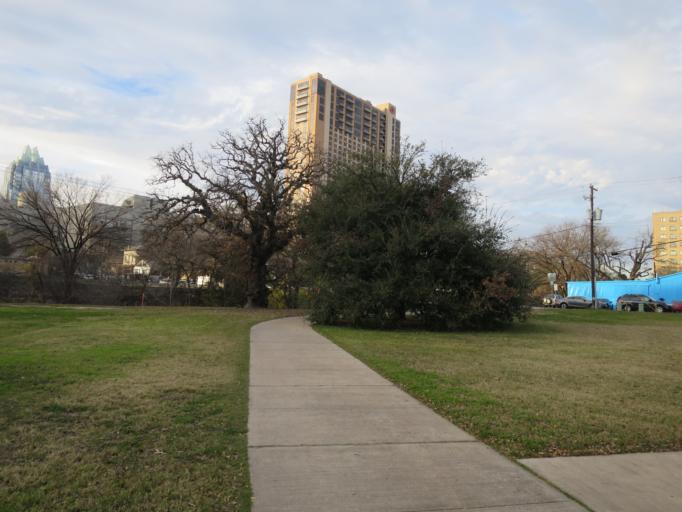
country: US
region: Texas
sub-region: Travis County
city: Austin
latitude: 30.2628
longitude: -97.7369
